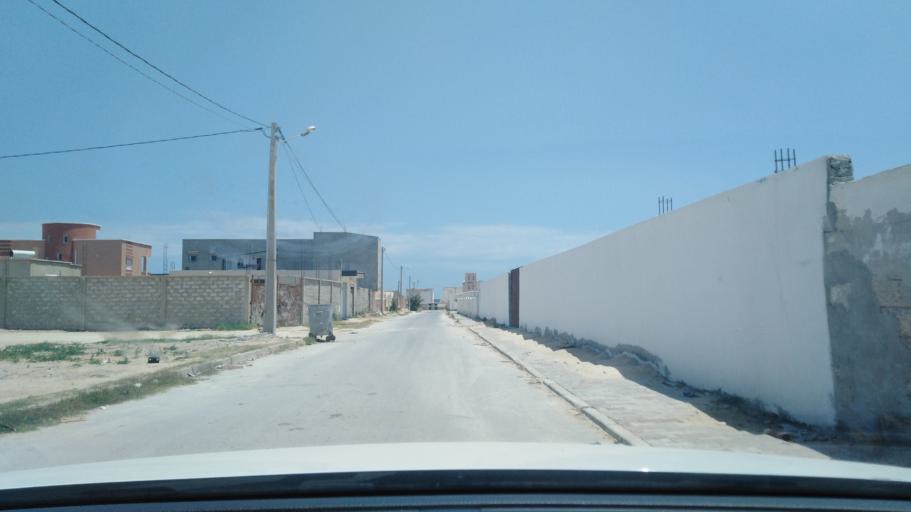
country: TN
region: Qabis
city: Gabes
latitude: 33.9502
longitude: 10.0697
